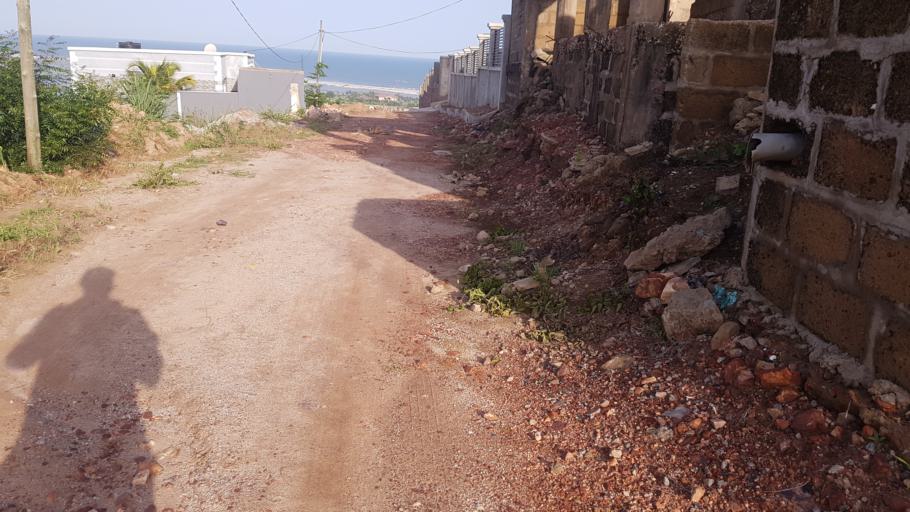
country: GH
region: Greater Accra
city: Gbawe
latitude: 5.5187
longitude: -0.3376
